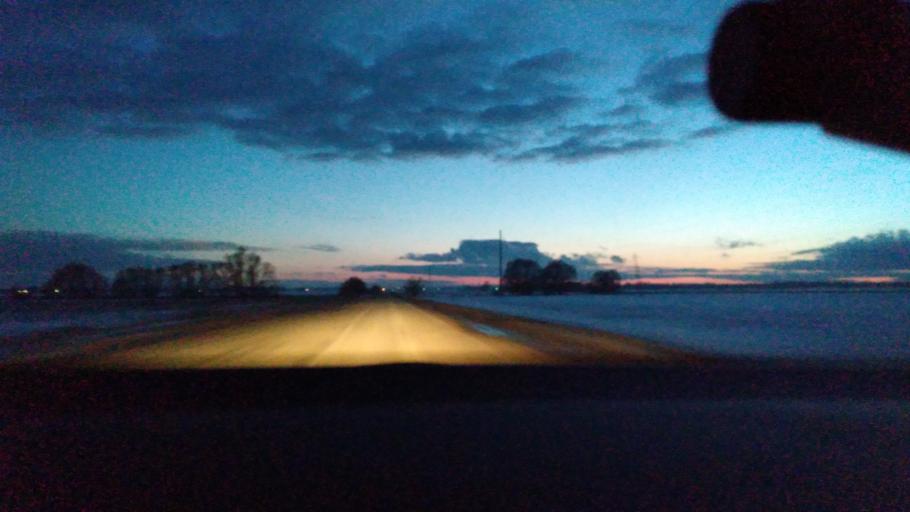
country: RU
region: Moskovskaya
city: Krasnaya Poyma
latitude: 55.0813
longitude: 39.1386
